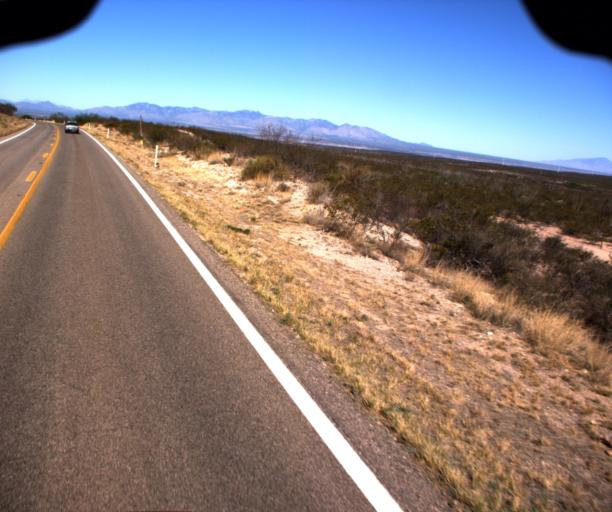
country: US
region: Arizona
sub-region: Cochise County
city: Tombstone
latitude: 31.7482
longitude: -110.1093
